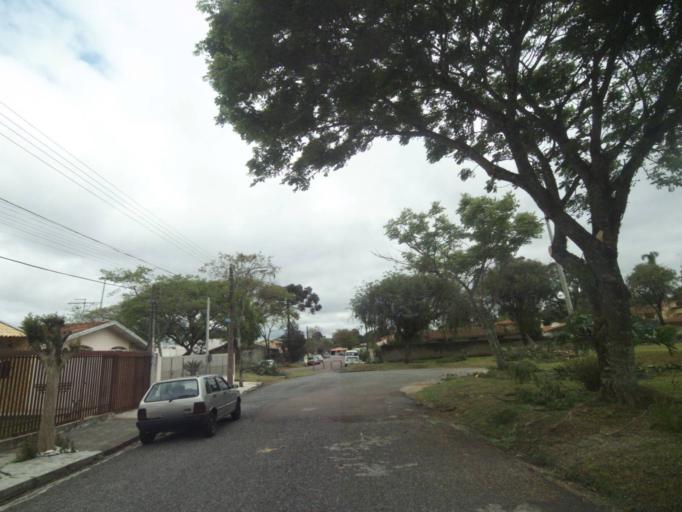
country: BR
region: Parana
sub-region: Pinhais
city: Pinhais
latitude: -25.3976
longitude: -49.2210
